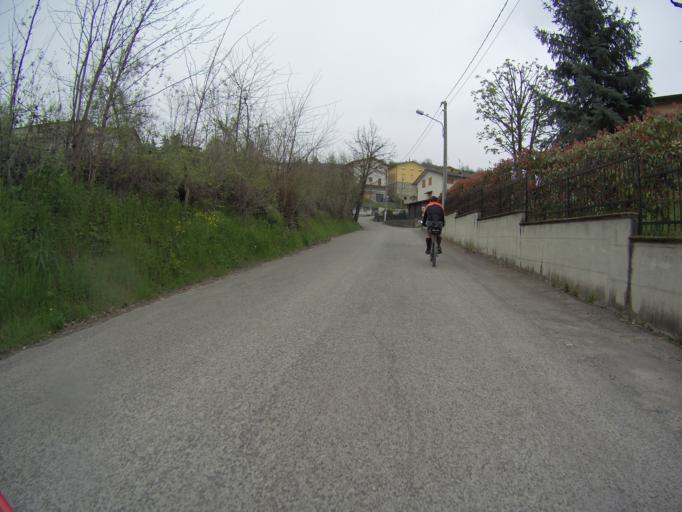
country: IT
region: Emilia-Romagna
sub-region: Provincia di Reggio Emilia
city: Ciano d'Enza
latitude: 44.5917
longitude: 10.4059
